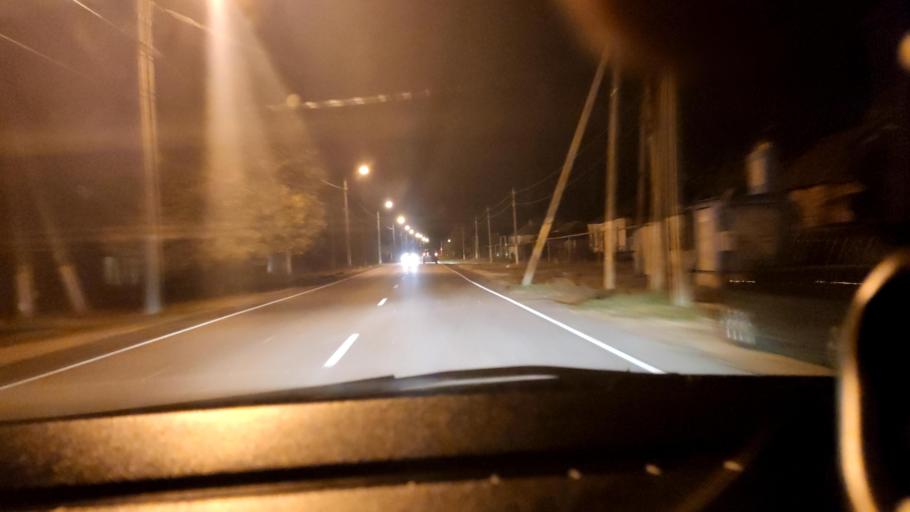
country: RU
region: Voronezj
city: Shilovo
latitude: 51.5746
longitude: 39.0403
